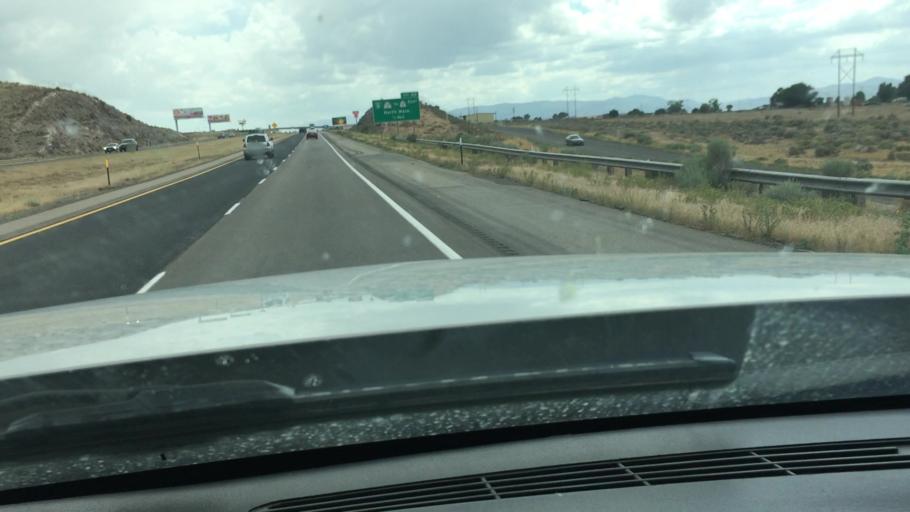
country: US
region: Utah
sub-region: Iron County
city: Enoch
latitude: 37.7389
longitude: -113.0425
